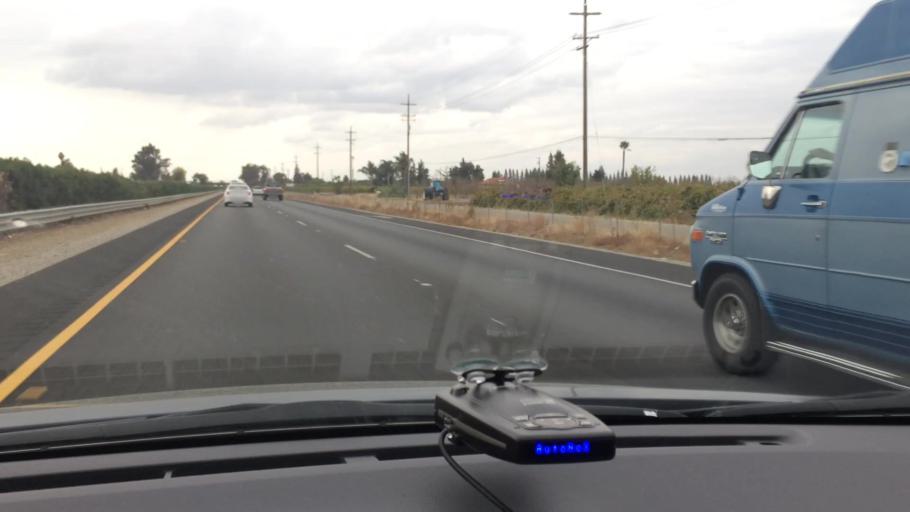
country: US
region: California
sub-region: San Joaquin County
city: Collierville
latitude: 38.1810
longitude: -121.2624
